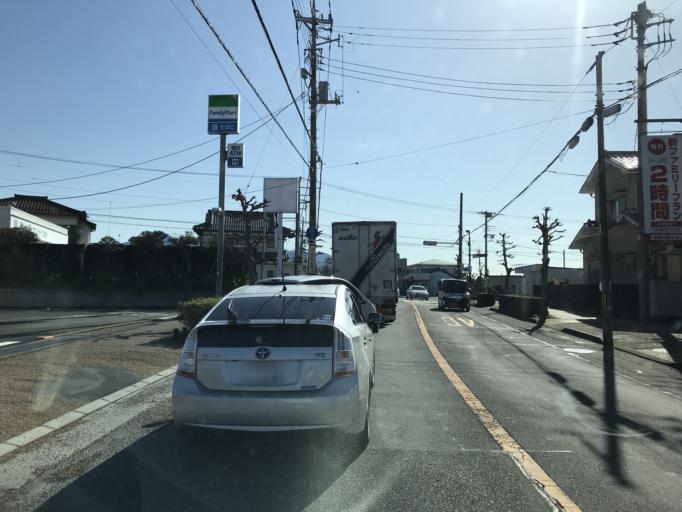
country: JP
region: Shizuoka
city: Fujinomiya
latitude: 35.2236
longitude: 138.6250
